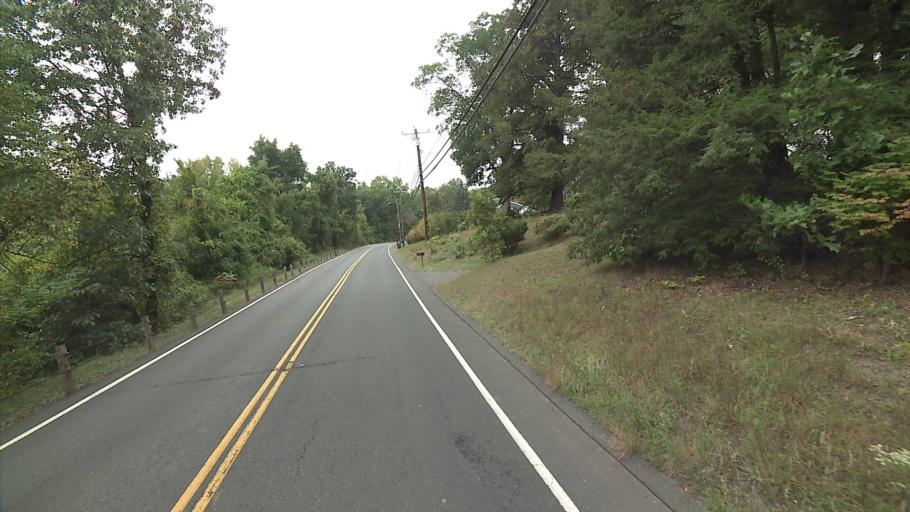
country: US
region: Connecticut
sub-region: Hartford County
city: Tariffville
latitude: 41.9035
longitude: -72.7738
